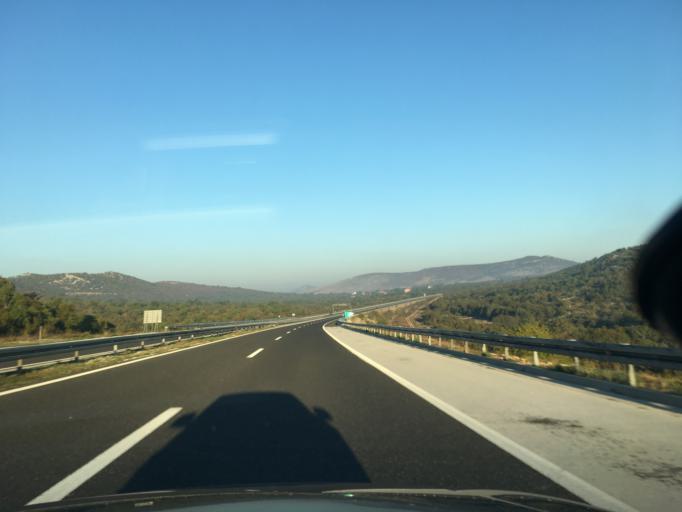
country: HR
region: Splitsko-Dalmatinska
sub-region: Grad Trogir
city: Trogir
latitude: 43.6325
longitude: 16.2233
